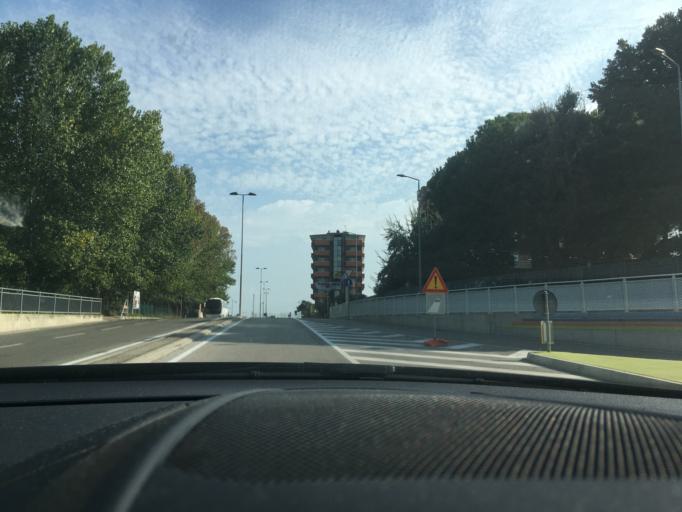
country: IT
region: Emilia-Romagna
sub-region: Provincia di Rimini
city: Bellaria-Igea Marina
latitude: 44.1120
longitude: 12.5029
